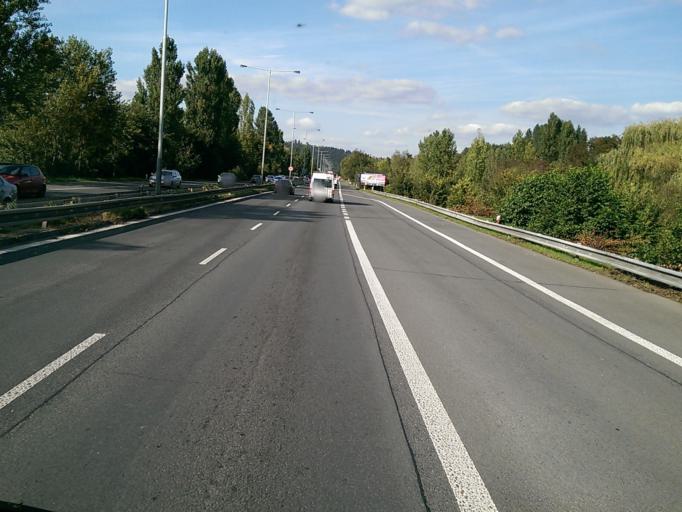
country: CZ
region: Praha
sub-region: Praha 12
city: Modrany
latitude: 50.0037
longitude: 14.3951
